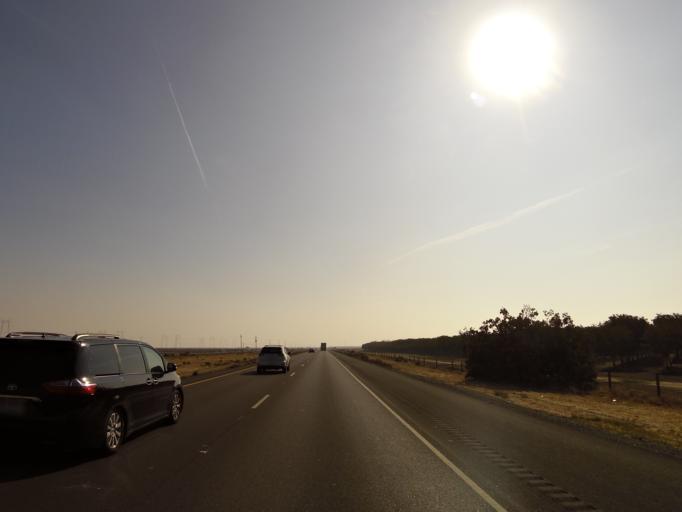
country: US
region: California
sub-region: Kings County
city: Kettleman City
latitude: 35.9052
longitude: -119.8823
